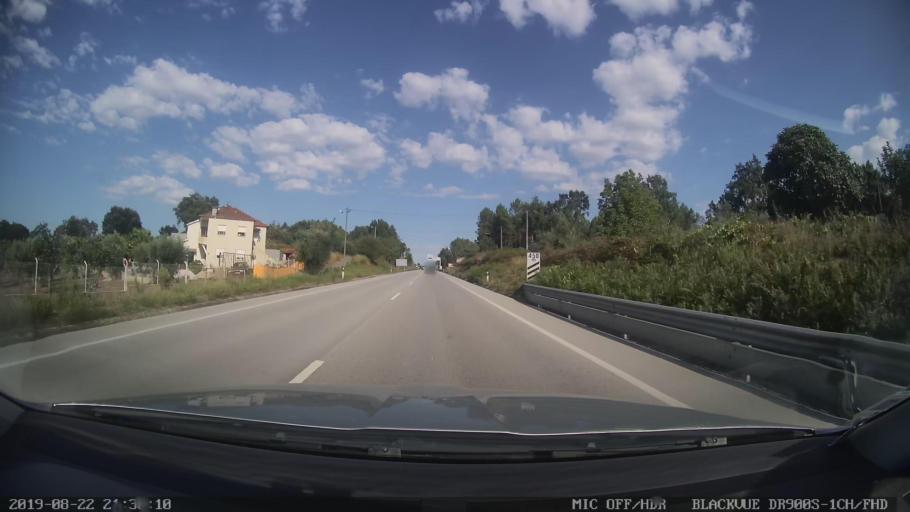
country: PT
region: Leiria
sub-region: Pedrogao Grande
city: Pedrogao Grande
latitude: 39.9078
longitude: -8.1469
